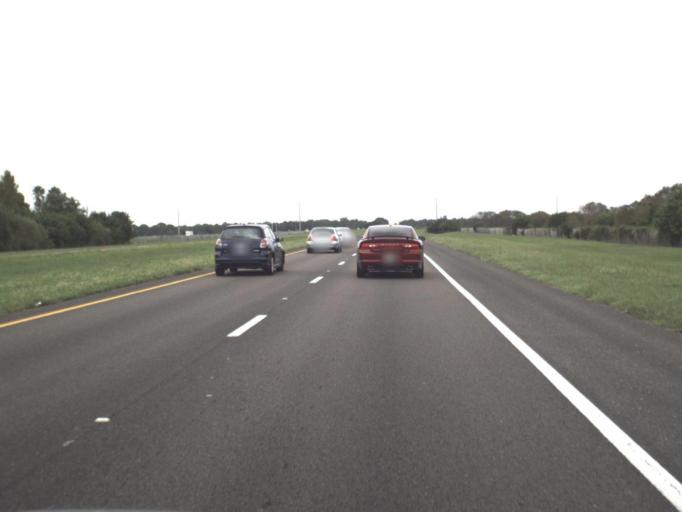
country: US
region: Florida
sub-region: Manatee County
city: Samoset
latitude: 27.4554
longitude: -82.5302
